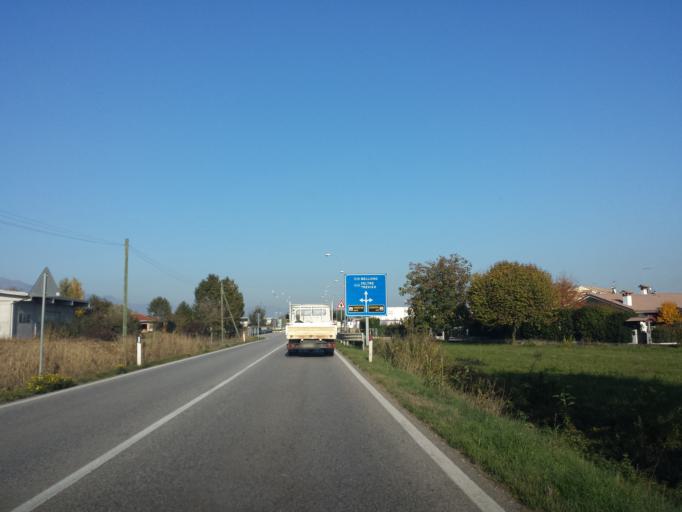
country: IT
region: Veneto
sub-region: Provincia di Treviso
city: Cornuda
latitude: 45.8067
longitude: 12.0062
